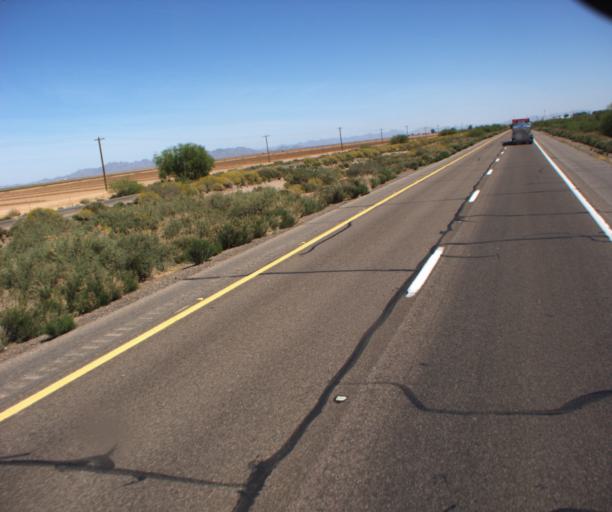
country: US
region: Arizona
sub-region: Maricopa County
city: Gila Bend
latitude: 32.9163
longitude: -112.9220
